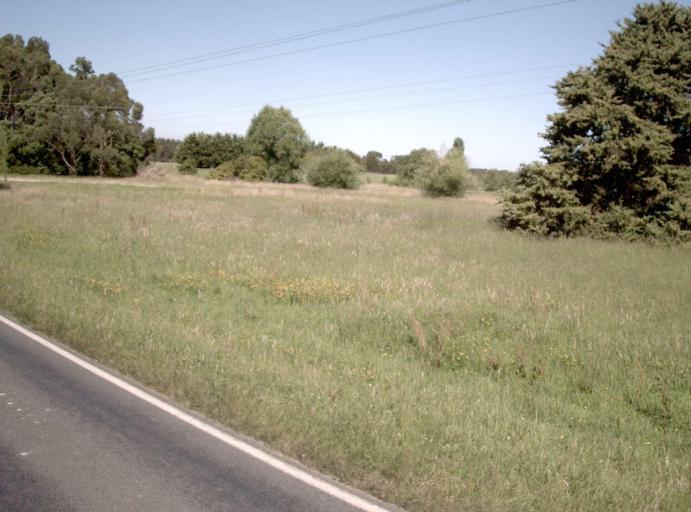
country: AU
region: Victoria
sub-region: Latrobe
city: Morwell
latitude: -38.6435
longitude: 146.4820
